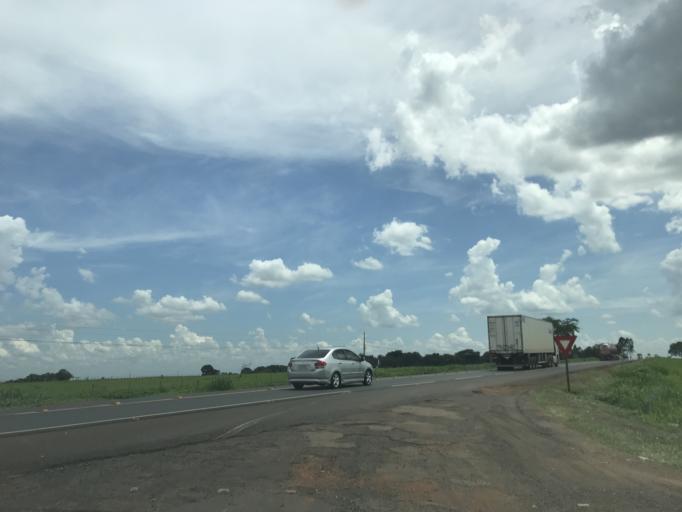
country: BR
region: Sao Paulo
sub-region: Nova Granada
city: Nova Granada
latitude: -20.2806
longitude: -49.1940
